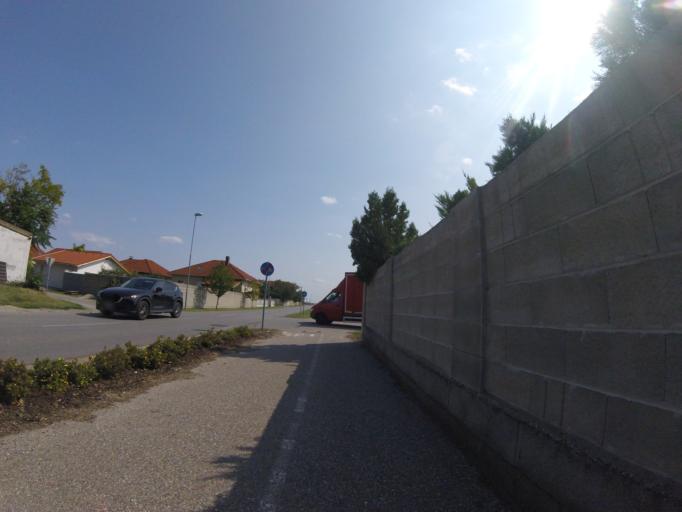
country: AT
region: Burgenland
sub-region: Politischer Bezirk Neusiedl am See
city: Apetlon
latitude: 47.7400
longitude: 16.8324
